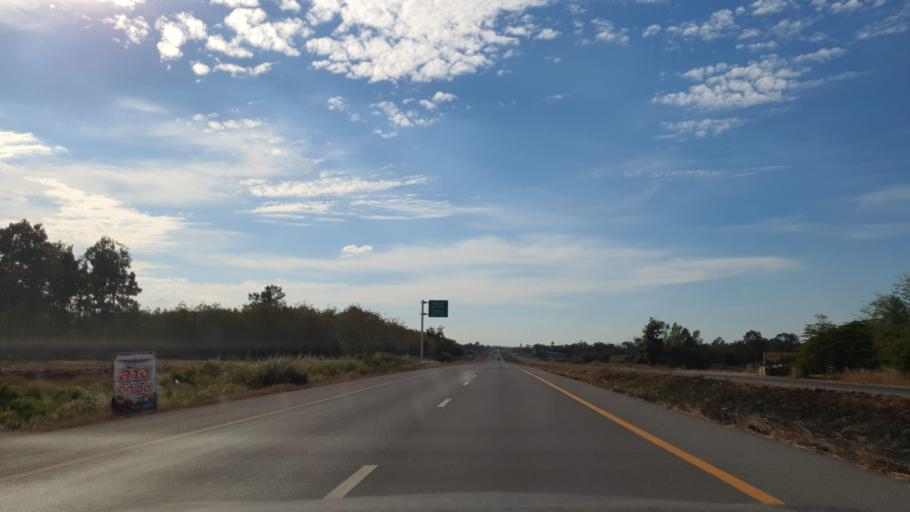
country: TH
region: Roi Et
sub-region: Amphoe Pho Chai
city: Pho Chai
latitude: 16.4124
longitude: 103.7683
